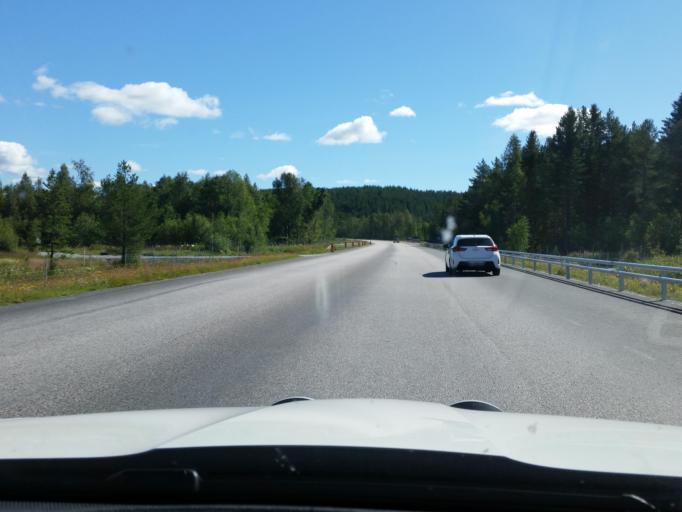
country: SE
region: Norrbotten
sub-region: Pitea Kommun
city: Bergsviken
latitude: 65.3146
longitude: 21.3402
